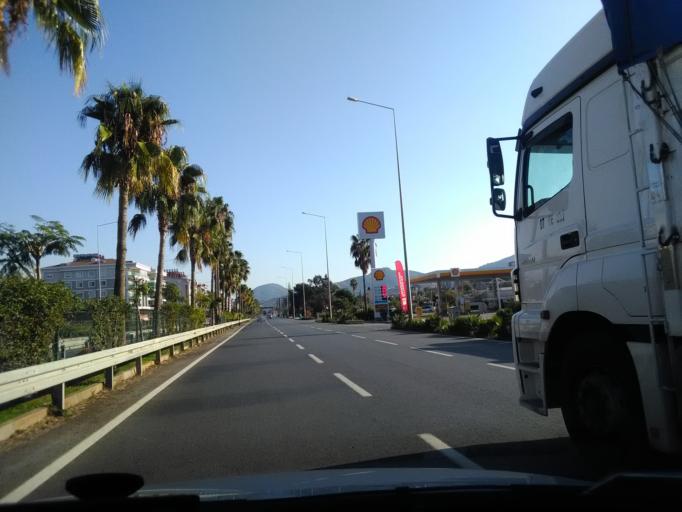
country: TR
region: Antalya
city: Gazipasa
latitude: 36.2801
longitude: 32.3028
